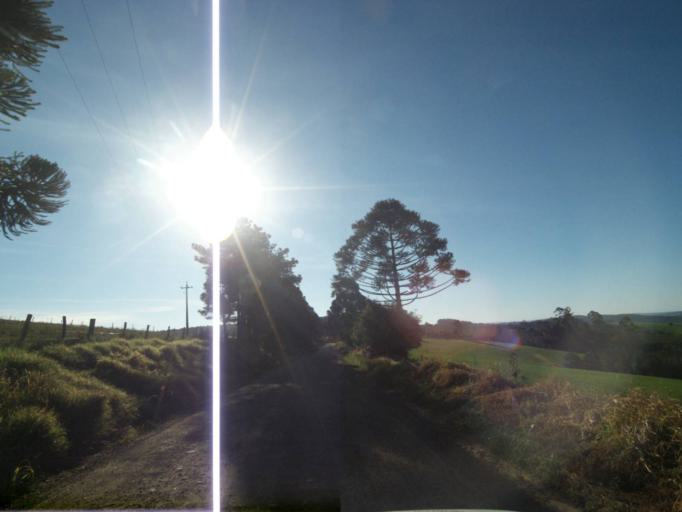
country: BR
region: Parana
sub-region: Telemaco Borba
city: Telemaco Borba
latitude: -24.5195
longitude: -50.6459
